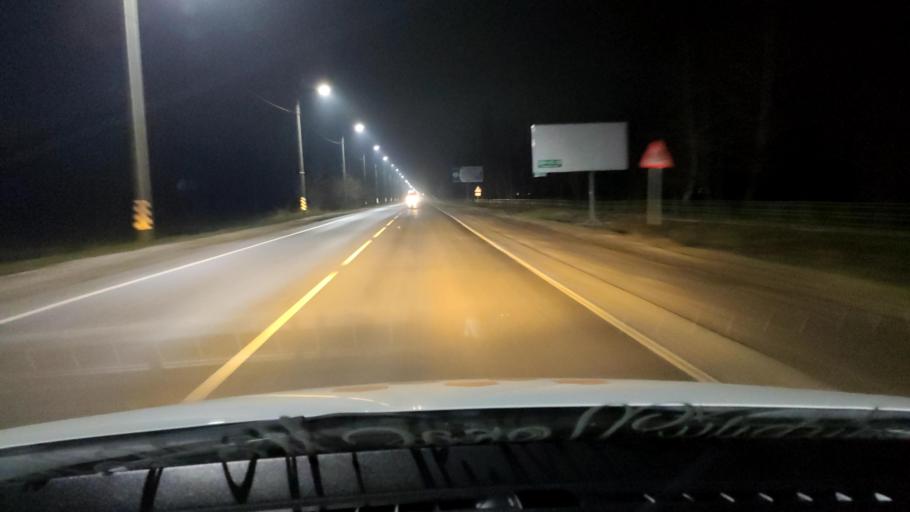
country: RU
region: Voronezj
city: Semiluki
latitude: 51.7279
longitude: 39.0370
